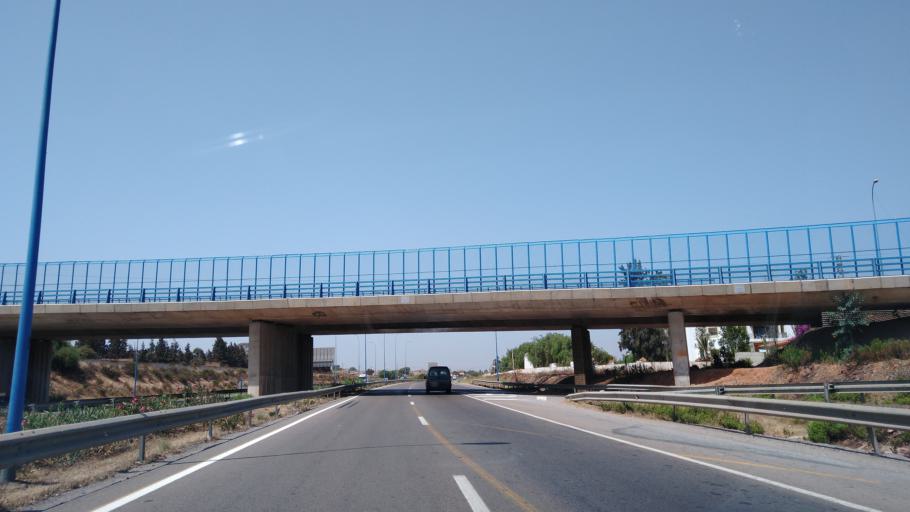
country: MA
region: Grand Casablanca
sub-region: Nouaceur
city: Bouskoura
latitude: 33.4997
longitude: -7.6302
